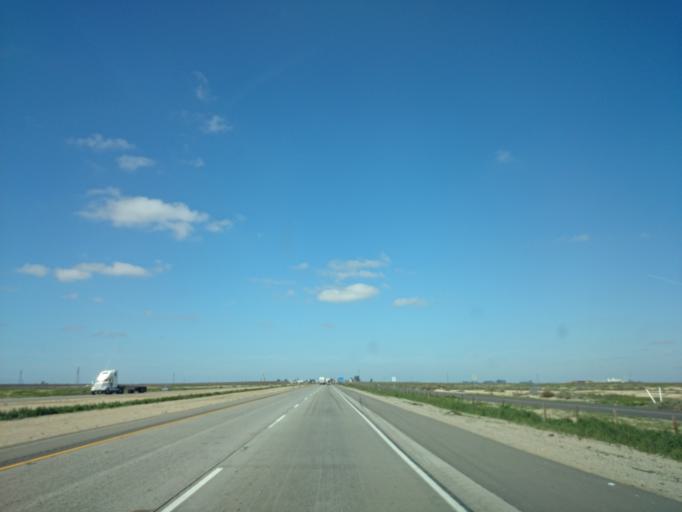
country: US
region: California
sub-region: Kern County
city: Buttonwillow
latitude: 35.4033
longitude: -119.4031
